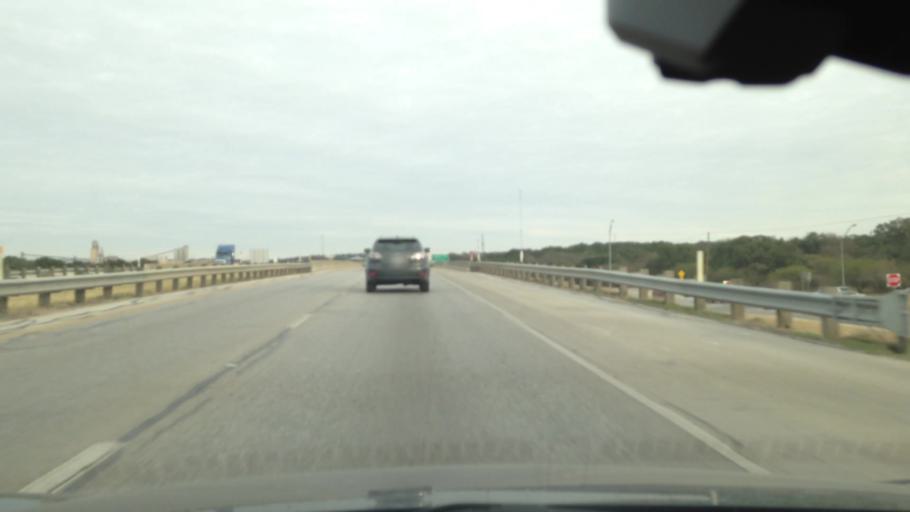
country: US
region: Texas
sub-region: Bexar County
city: Live Oak
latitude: 29.6025
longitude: -98.4065
